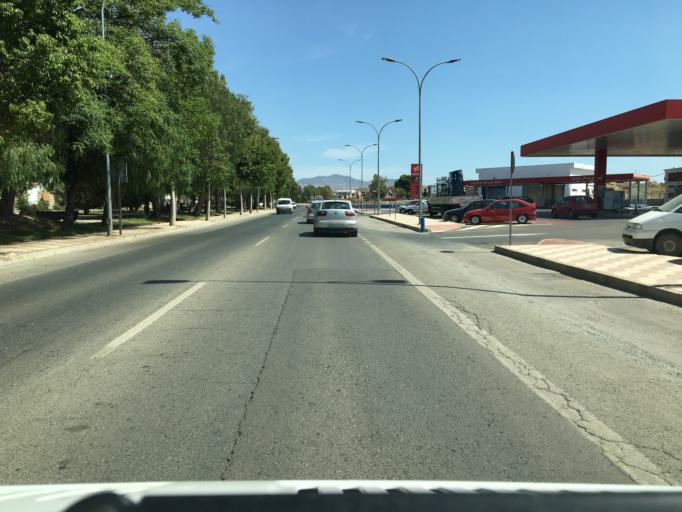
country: ES
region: Andalusia
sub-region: Provincia de Almeria
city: Huercal-Overa
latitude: 37.4010
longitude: -1.9389
